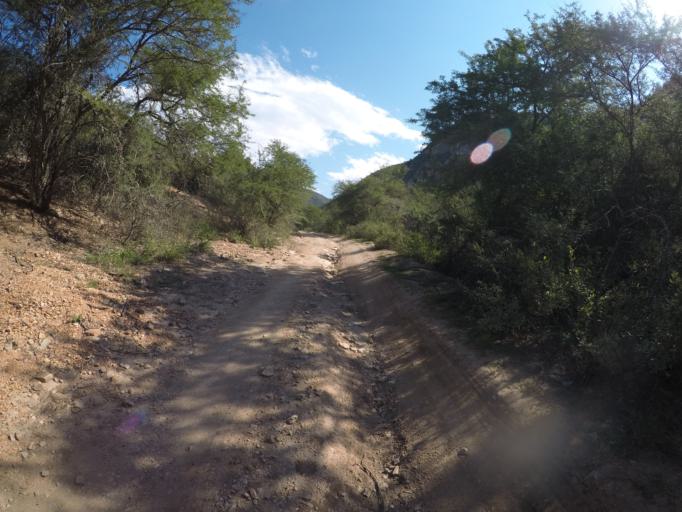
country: ZA
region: Eastern Cape
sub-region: Cacadu District Municipality
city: Kareedouw
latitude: -33.6546
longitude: 24.3645
